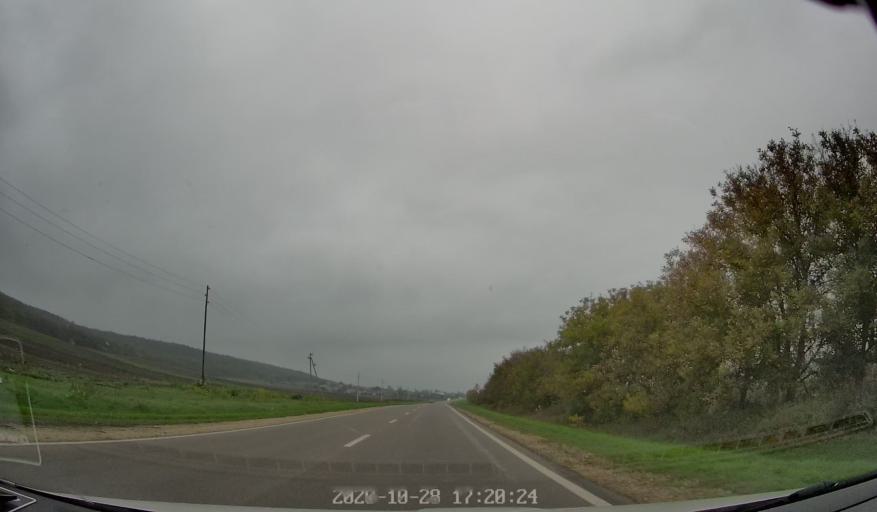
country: MD
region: Cimislia
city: Cimislia
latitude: 46.5688
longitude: 28.7569
